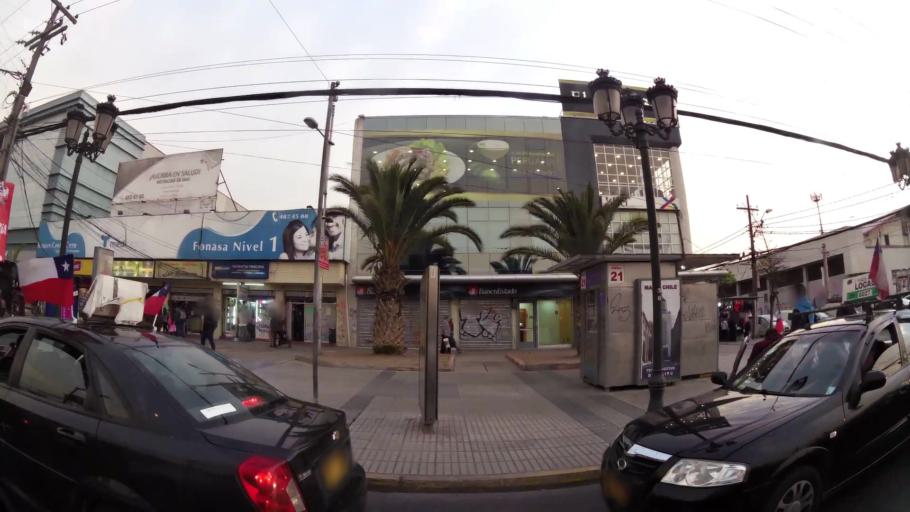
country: CL
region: Santiago Metropolitan
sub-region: Provincia de Santiago
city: Lo Prado
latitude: -33.5107
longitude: -70.7597
